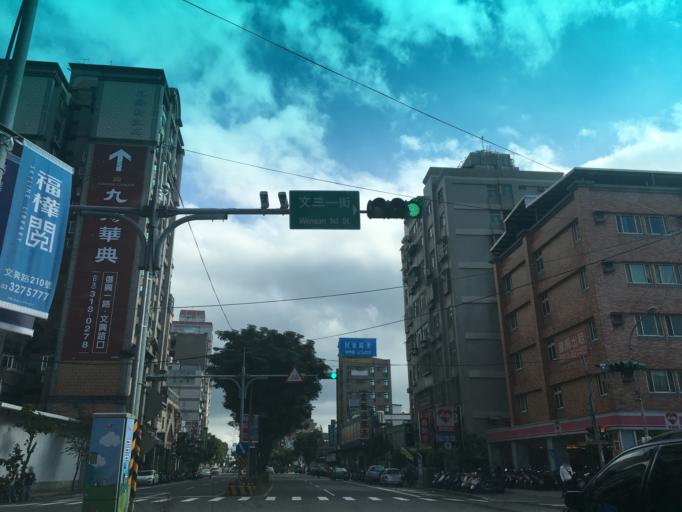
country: TW
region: Taiwan
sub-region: Taoyuan
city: Taoyuan
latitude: 25.0598
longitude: 121.3623
